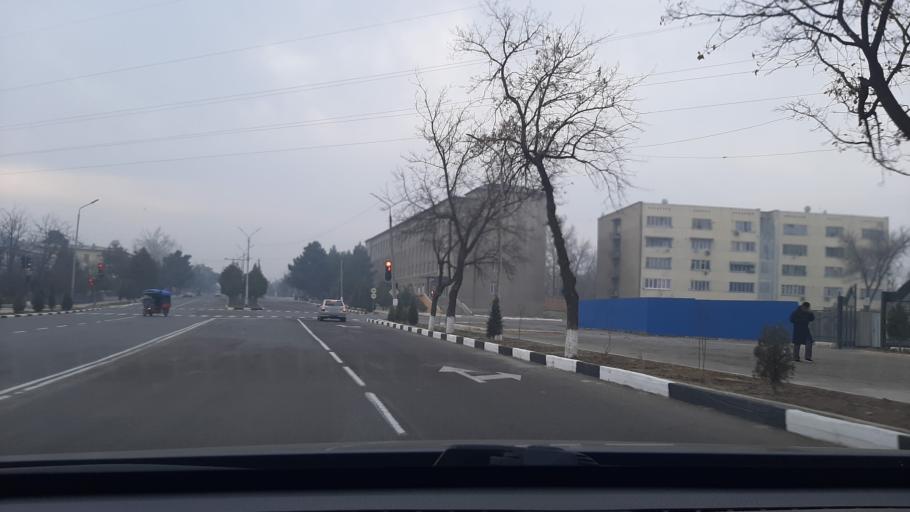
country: TJ
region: Viloyati Sughd
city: Chkalov
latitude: 40.2358
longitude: 69.6883
